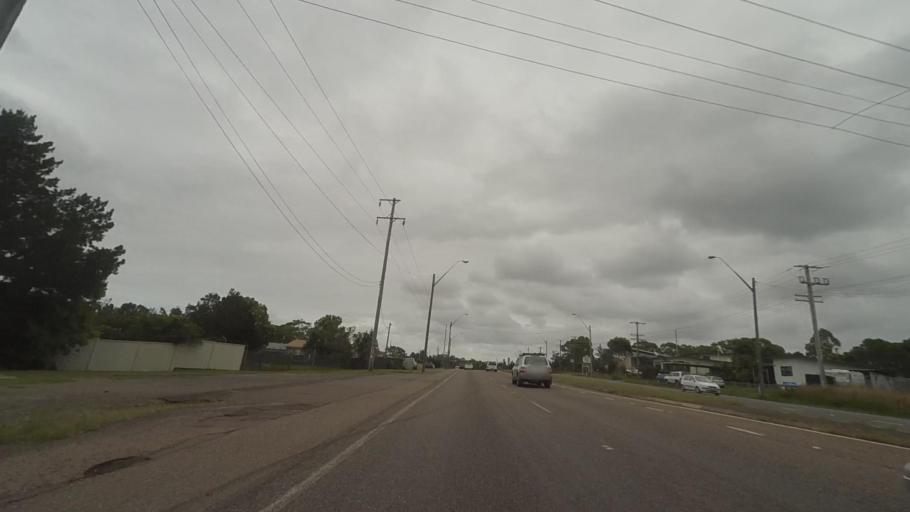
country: AU
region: New South Wales
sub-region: Wyong Shire
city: Buff Point
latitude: -33.1978
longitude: 151.5244
